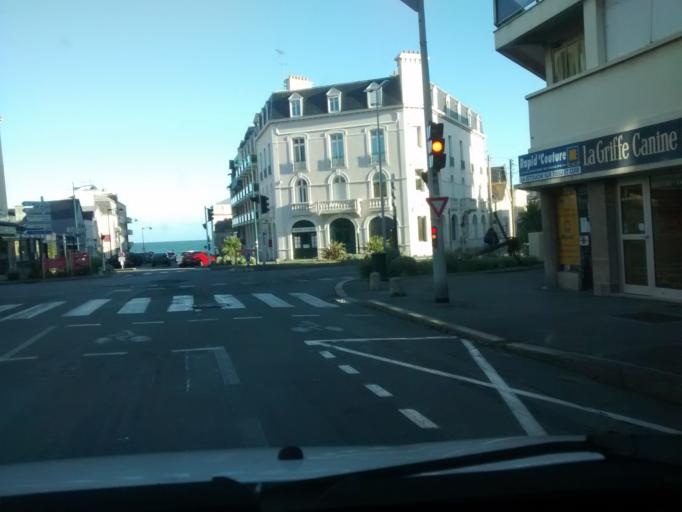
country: FR
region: Brittany
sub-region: Departement d'Ille-et-Vilaine
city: Saint-Malo
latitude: 48.6625
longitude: -1.9884
